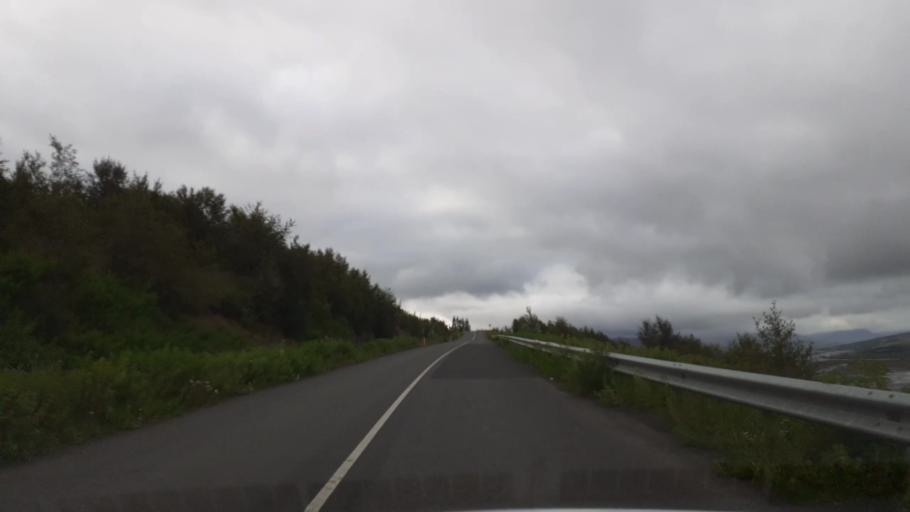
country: IS
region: Northeast
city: Akureyri
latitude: 65.6826
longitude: -18.0427
